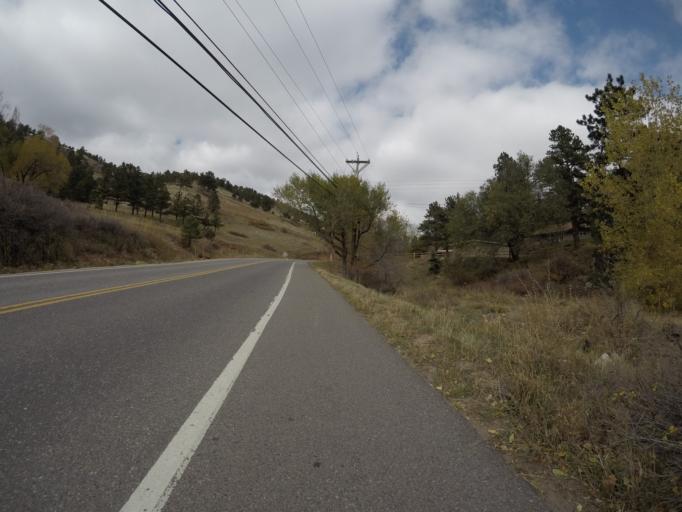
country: US
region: Colorado
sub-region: Boulder County
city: Boulder
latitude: 40.0662
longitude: -105.3019
